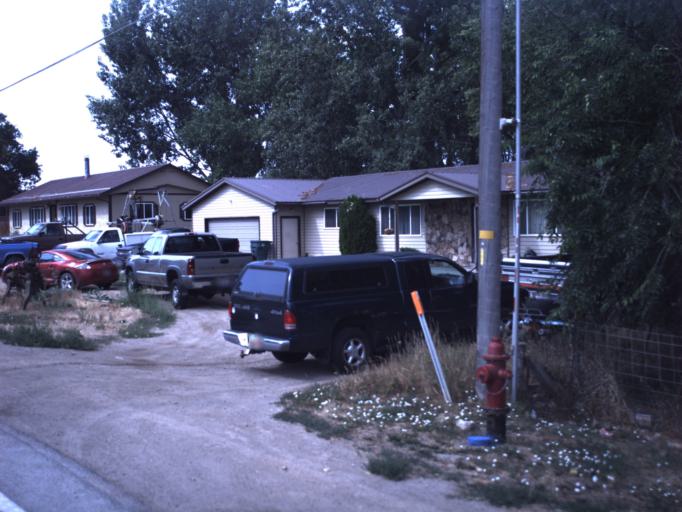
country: US
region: Utah
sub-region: Uintah County
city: Naples
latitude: 40.3948
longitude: -109.4989
